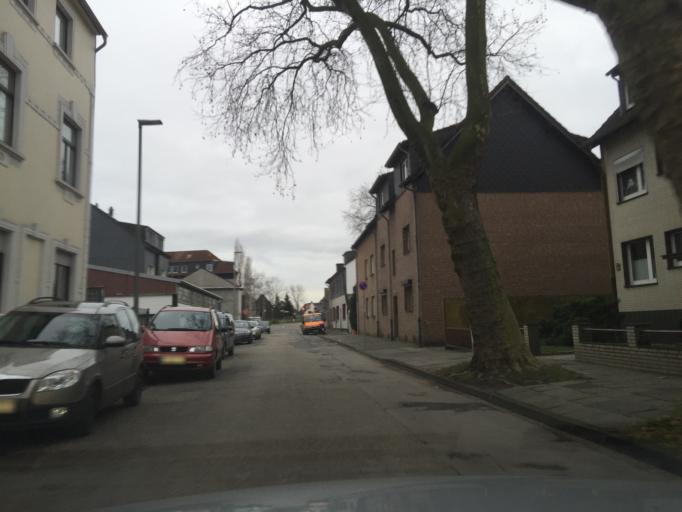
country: DE
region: North Rhine-Westphalia
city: Meiderich
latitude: 51.4695
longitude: 6.8208
